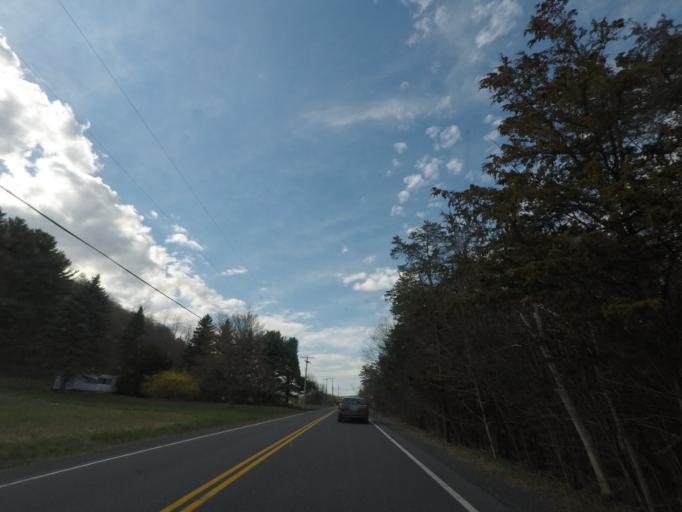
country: US
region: New York
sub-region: Albany County
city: Voorheesville
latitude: 42.5635
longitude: -73.9522
